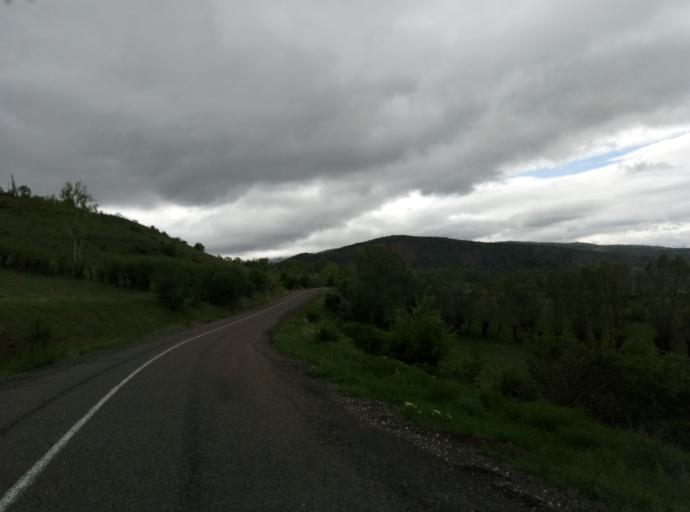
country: TR
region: Sivas
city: Aksu
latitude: 40.1880
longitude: 37.9450
